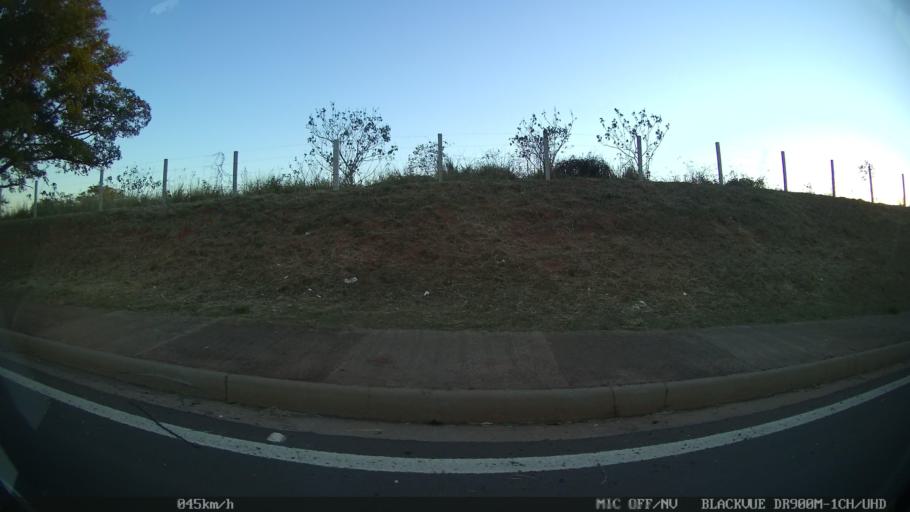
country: BR
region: Sao Paulo
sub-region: Sao Jose Do Rio Preto
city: Sao Jose do Rio Preto
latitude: -20.8515
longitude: -49.3935
